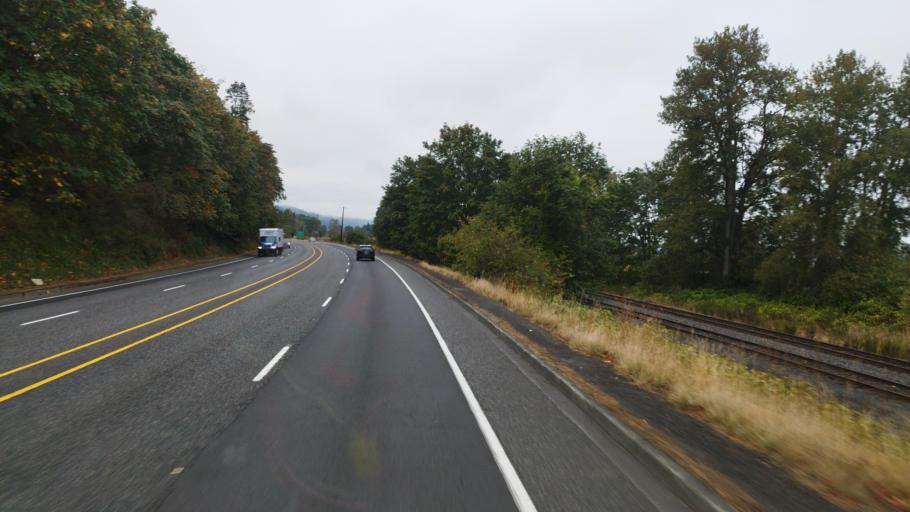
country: US
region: Oregon
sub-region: Columbia County
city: Rainier
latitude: 46.0931
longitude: -122.9475
